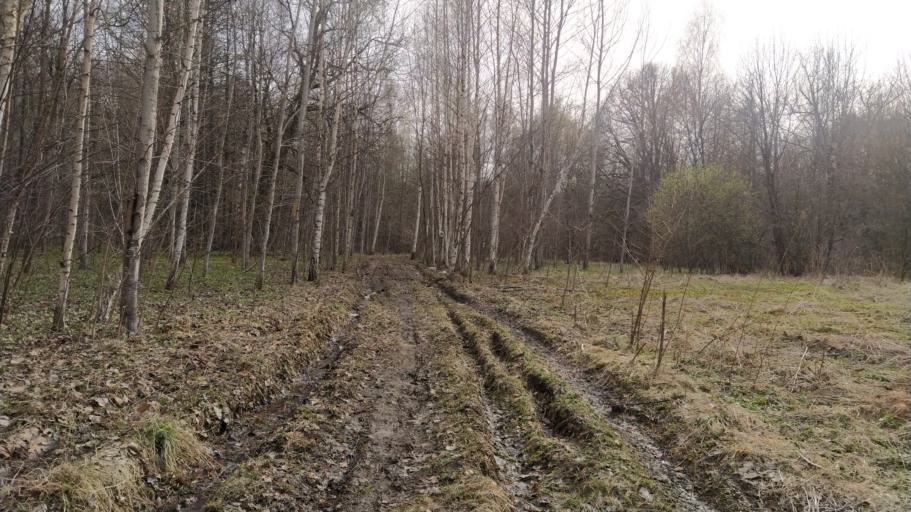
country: RU
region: Chuvashia
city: Novyye Lapsary
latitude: 56.1375
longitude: 47.1180
